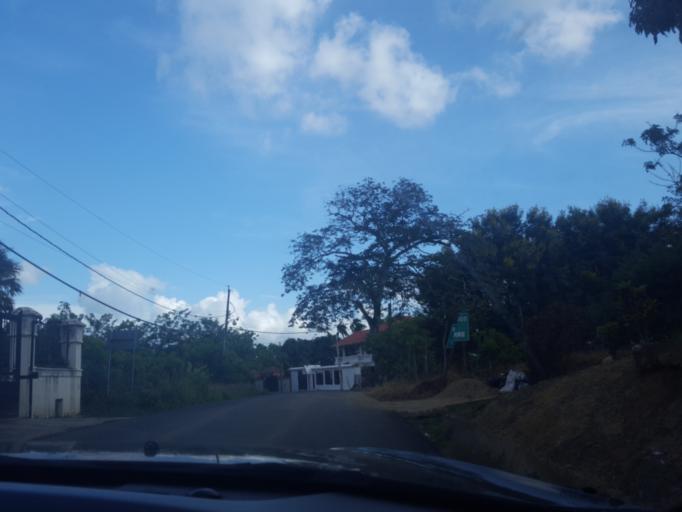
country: DO
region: La Vega
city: Rio Verde Arriba
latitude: 19.3540
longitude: -70.6296
